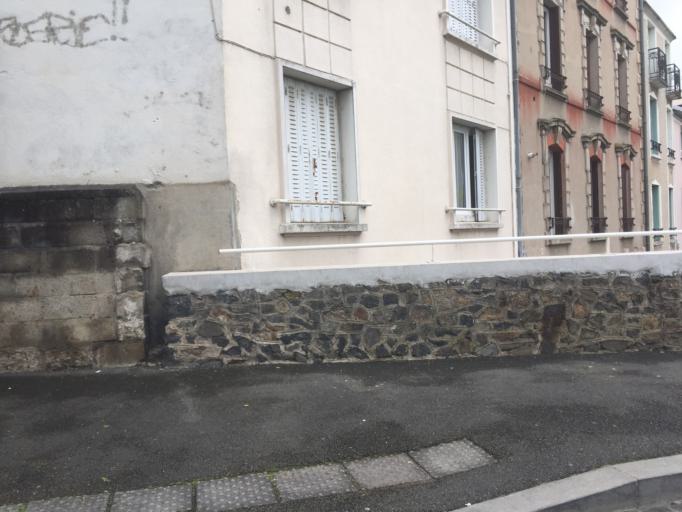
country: FR
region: Auvergne
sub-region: Departement de l'Allier
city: Vichy
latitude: 46.1245
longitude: 3.4309
